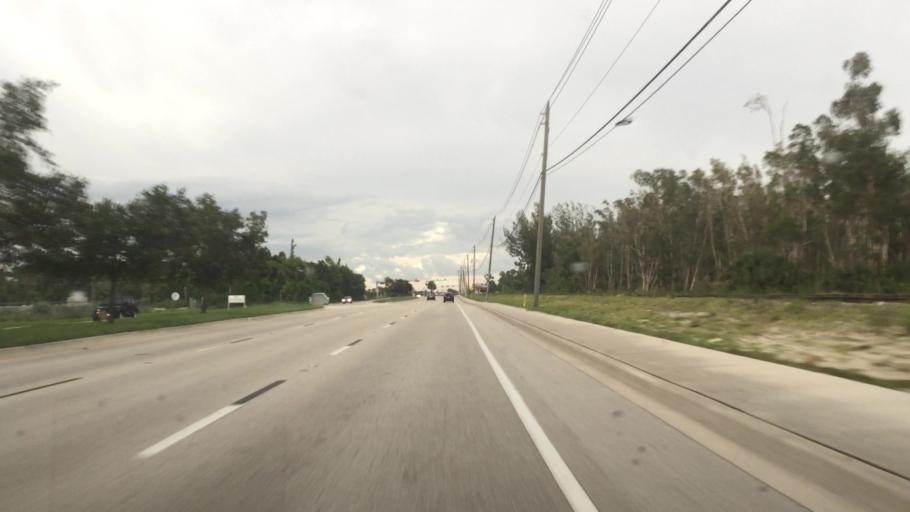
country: US
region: Florida
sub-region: Lee County
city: San Carlos Park
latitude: 26.4925
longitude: -81.8370
